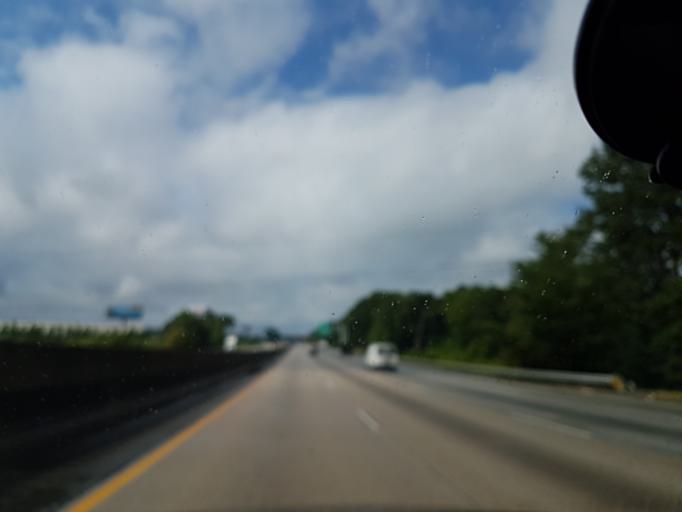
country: US
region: Georgia
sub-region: Fulton County
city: Union City
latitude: 33.5798
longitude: -84.5195
